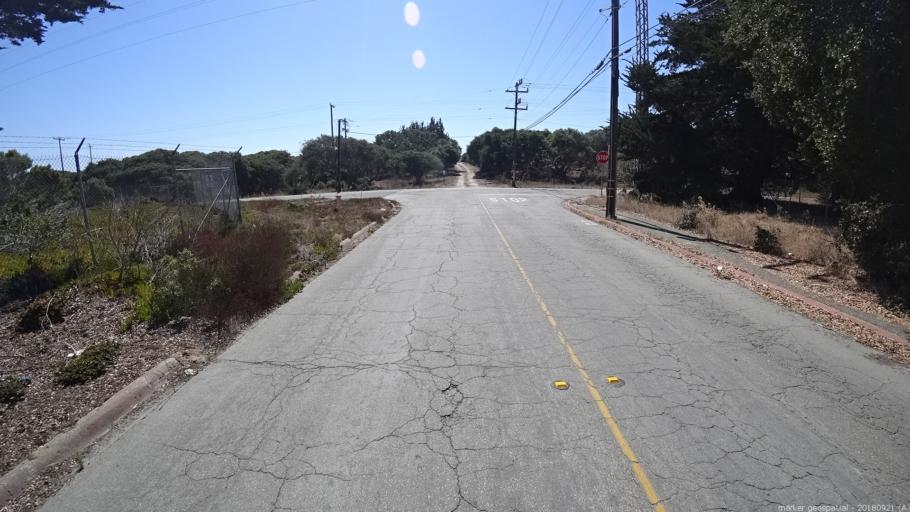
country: US
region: California
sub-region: Monterey County
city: Marina
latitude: 36.6441
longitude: -121.7899
